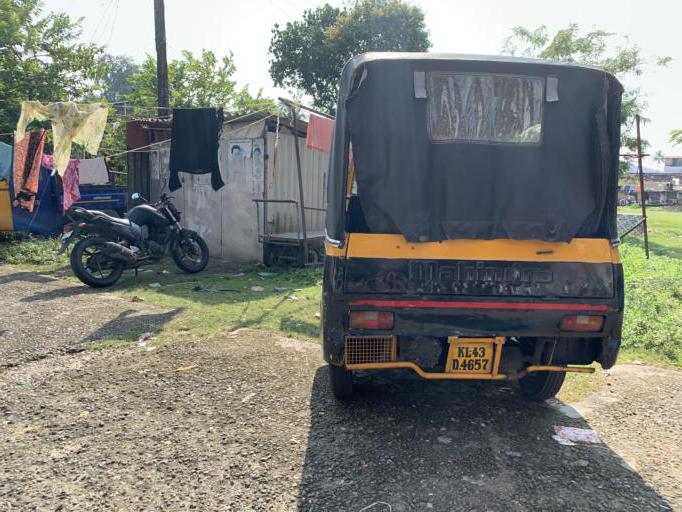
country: IN
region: Kerala
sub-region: Ernakulam
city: Cochin
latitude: 9.9625
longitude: 76.2547
